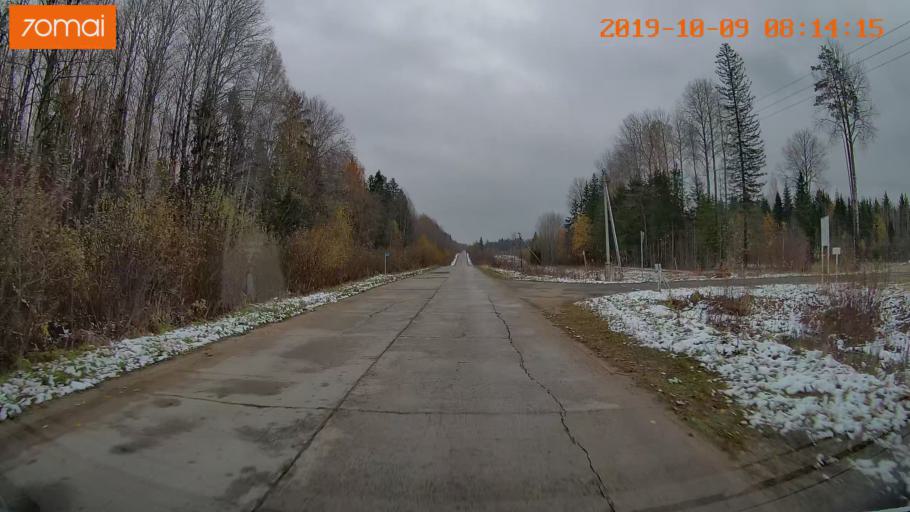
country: RU
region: Vologda
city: Gryazovets
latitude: 58.7277
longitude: 40.1529
